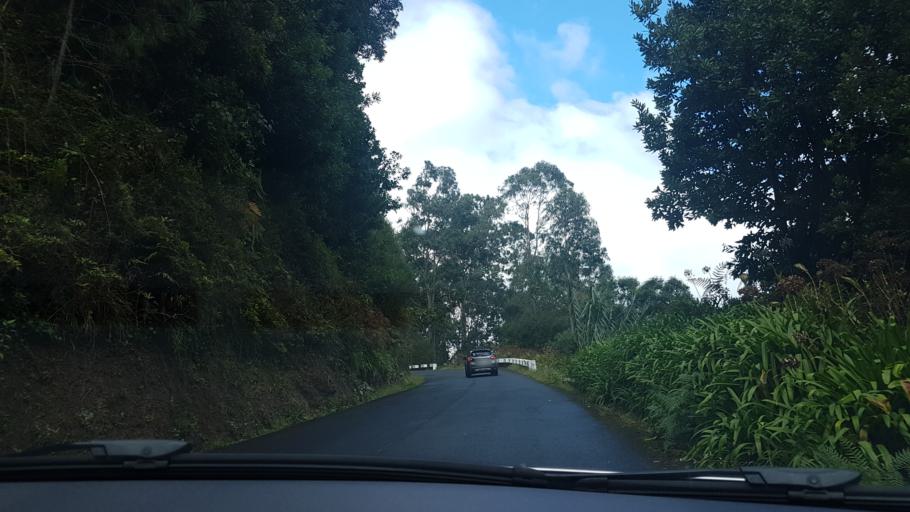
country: PT
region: Madeira
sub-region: Sao Vicente
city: Sao Vicente
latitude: 32.7656
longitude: -17.0271
